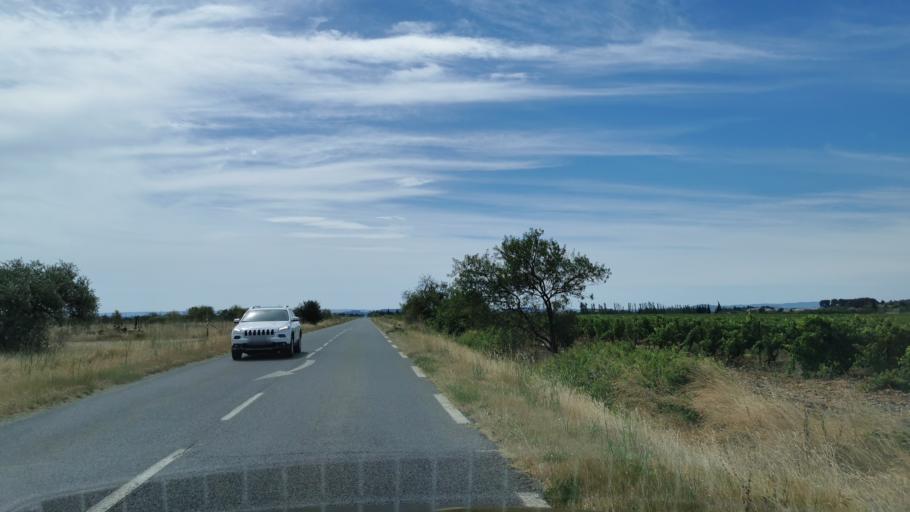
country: FR
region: Languedoc-Roussillon
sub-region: Departement de l'Aude
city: Ginestas
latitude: 43.2845
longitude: 2.8737
